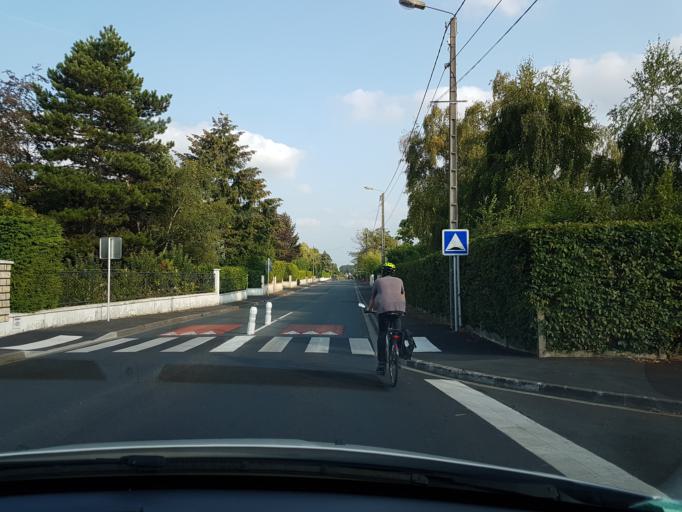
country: FR
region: Centre
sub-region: Departement d'Indre-et-Loire
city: Saint-Avertin
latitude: 47.3642
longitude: 0.7496
